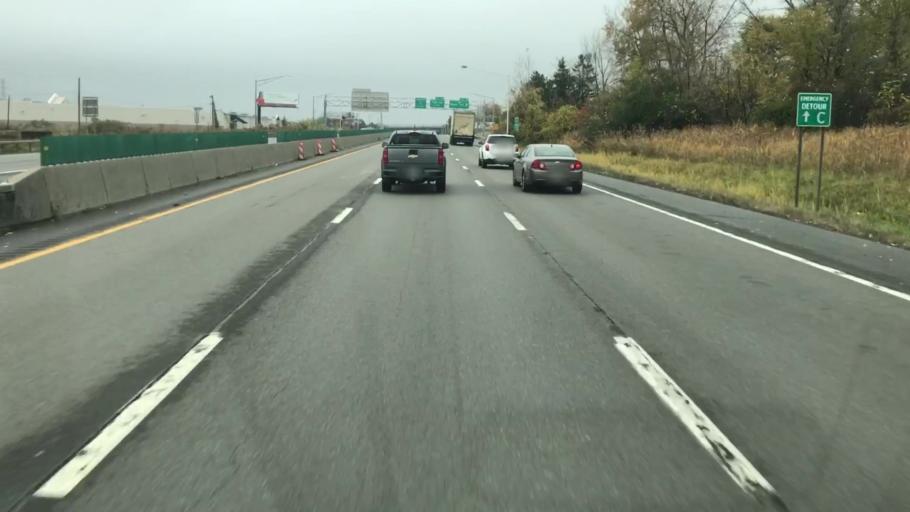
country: US
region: New York
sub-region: Onondaga County
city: East Syracuse
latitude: 43.0593
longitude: -76.0967
